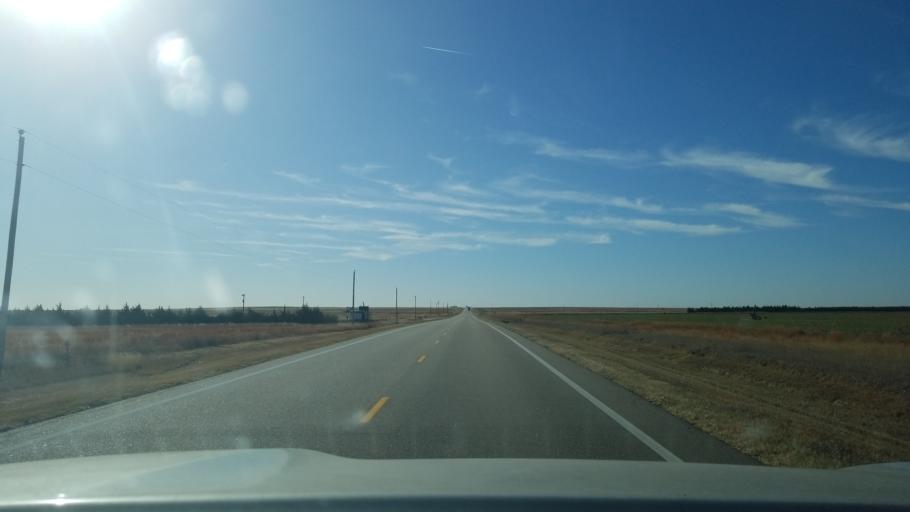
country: US
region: Kansas
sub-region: Ness County
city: Ness City
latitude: 38.3595
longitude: -99.8979
